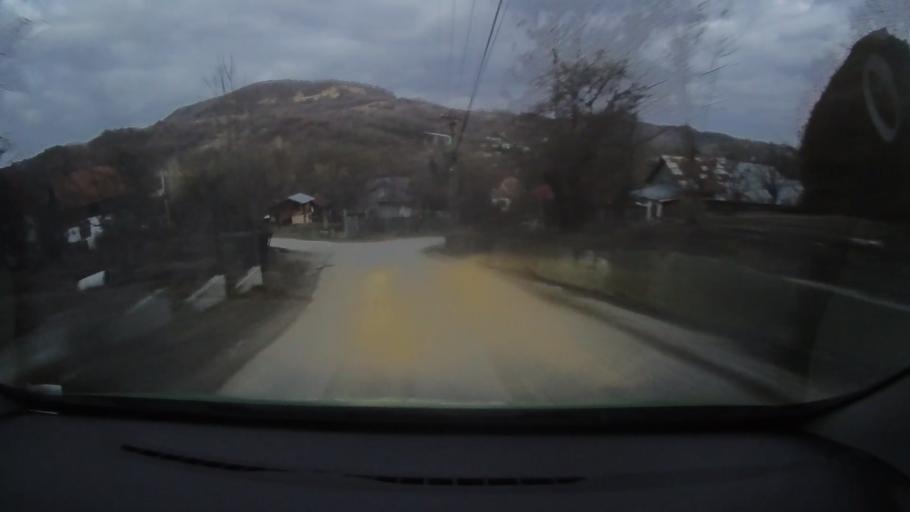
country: RO
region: Prahova
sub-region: Comuna Provita de Sus
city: Provita de Sus
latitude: 45.1398
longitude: 25.6290
